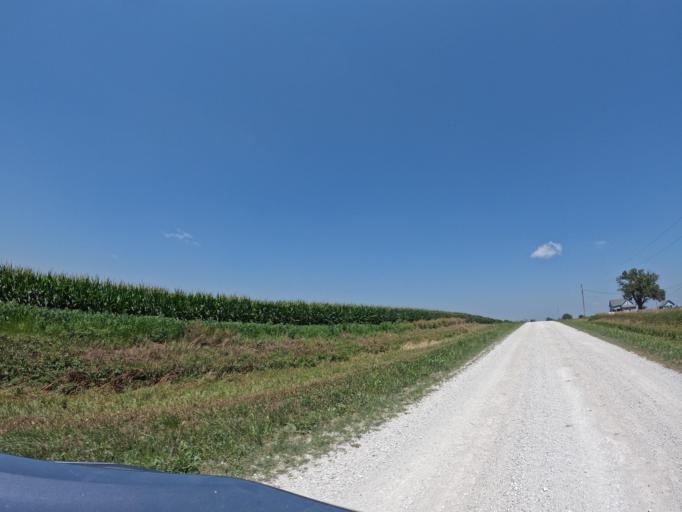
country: US
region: Iowa
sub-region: Keokuk County
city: Sigourney
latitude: 41.2639
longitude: -92.1699
